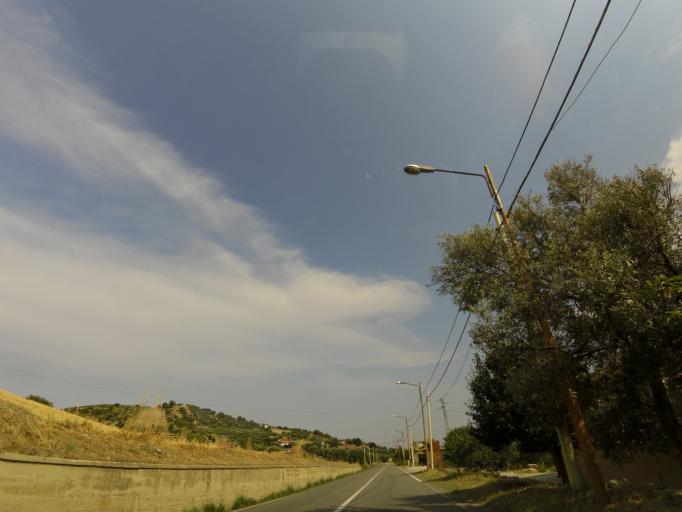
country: IT
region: Calabria
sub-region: Provincia di Reggio Calabria
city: Monasterace
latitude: 38.4432
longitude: 16.5404
